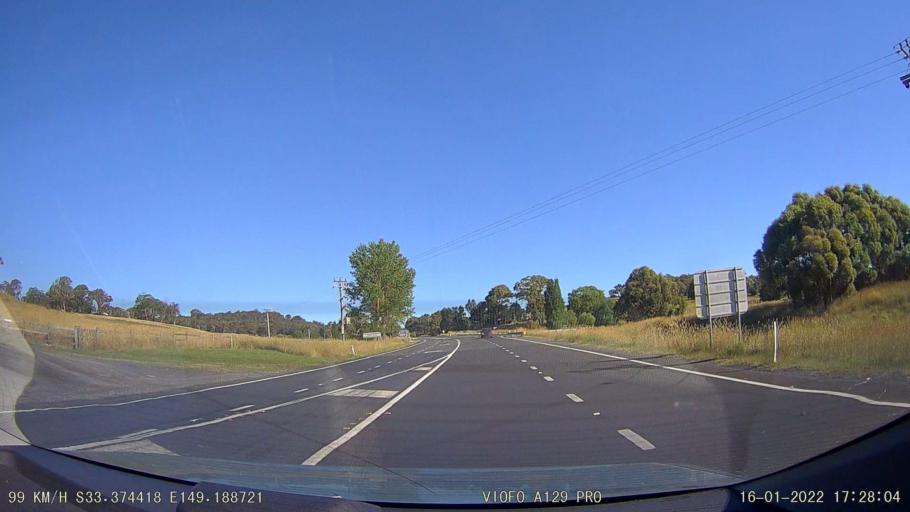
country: AU
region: New South Wales
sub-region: Blayney
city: Millthorpe
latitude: -33.3739
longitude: 149.1880
